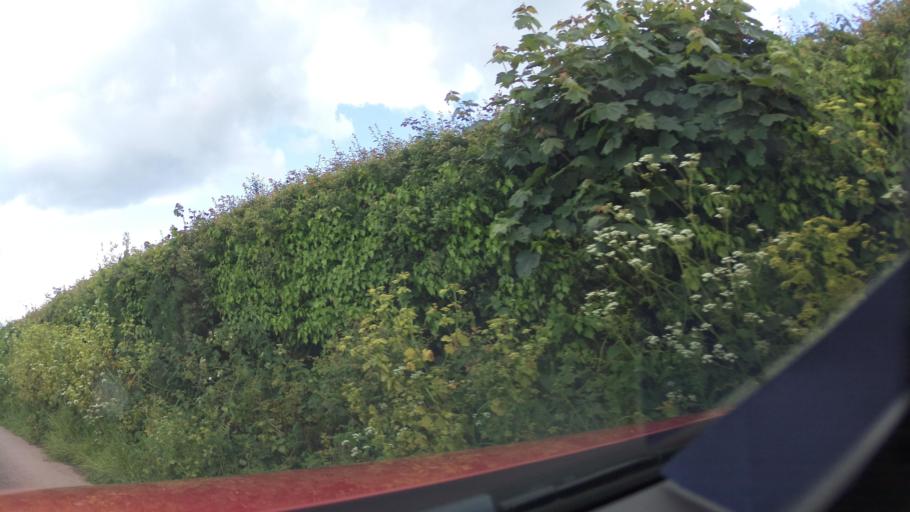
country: GB
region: England
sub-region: Devon
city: Dartmouth
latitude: 50.3557
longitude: -3.5468
